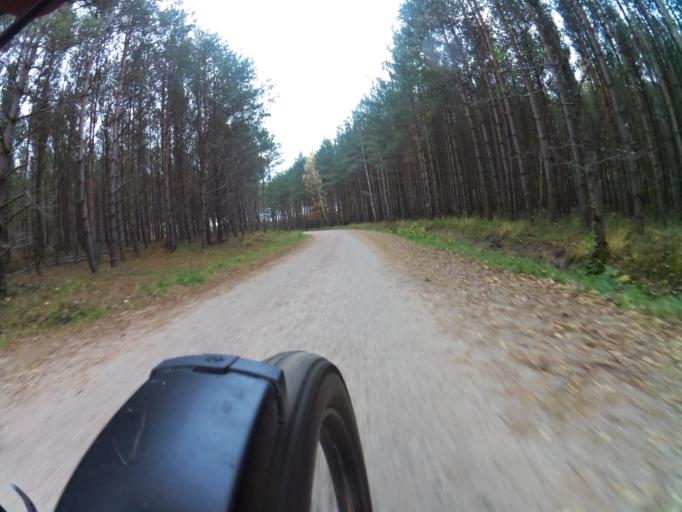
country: PL
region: Pomeranian Voivodeship
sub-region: Powiat wejherowski
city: Choczewo
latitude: 54.7816
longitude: 17.7349
